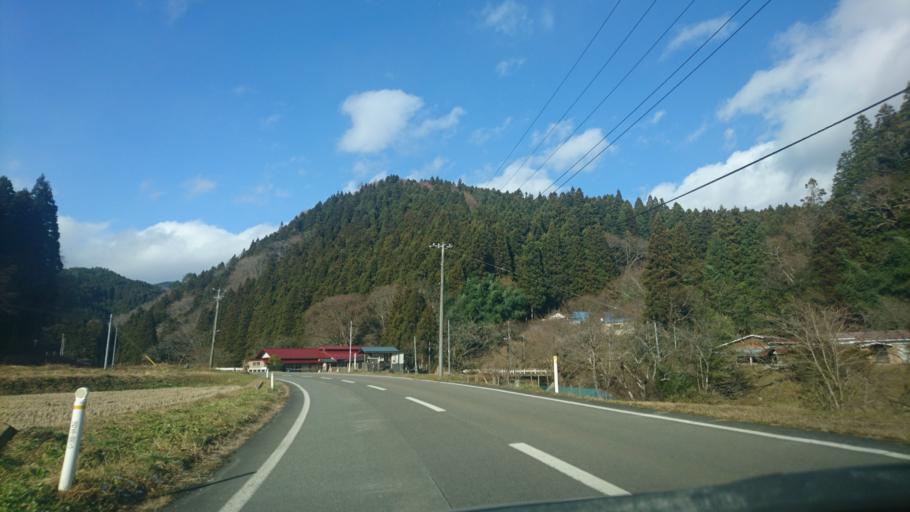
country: JP
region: Iwate
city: Mizusawa
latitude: 39.0838
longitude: 141.3909
